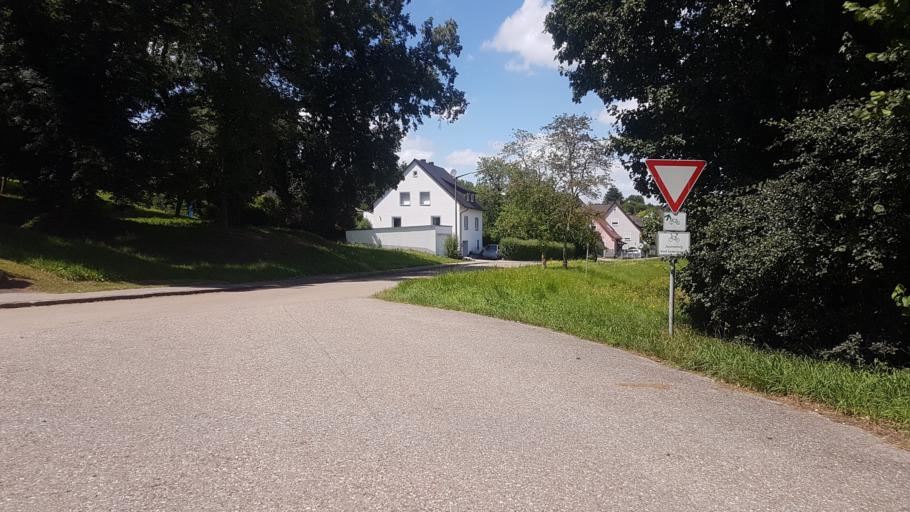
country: DE
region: Bavaria
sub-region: Regierungsbezirk Mittelfranken
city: Leutershausen
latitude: 49.3095
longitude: 10.3903
